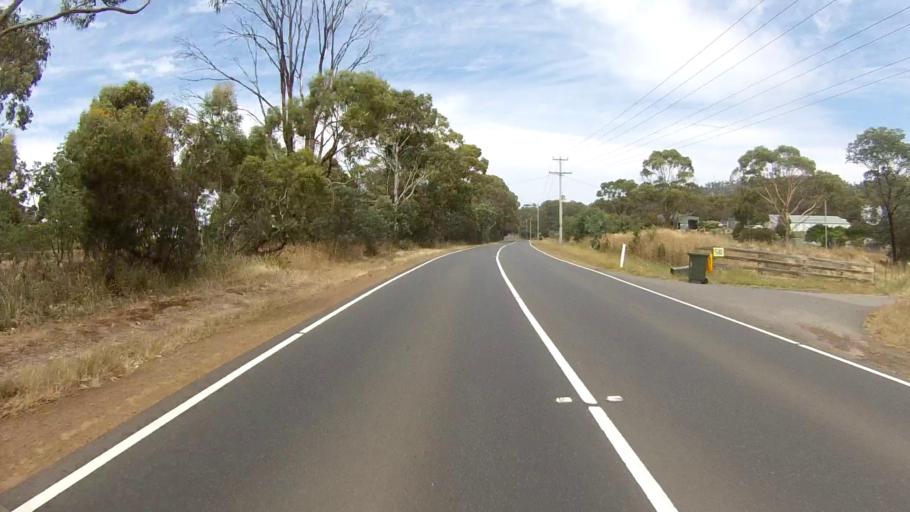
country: AU
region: Tasmania
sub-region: Clarence
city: Acton Park
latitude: -42.8761
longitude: 147.4828
